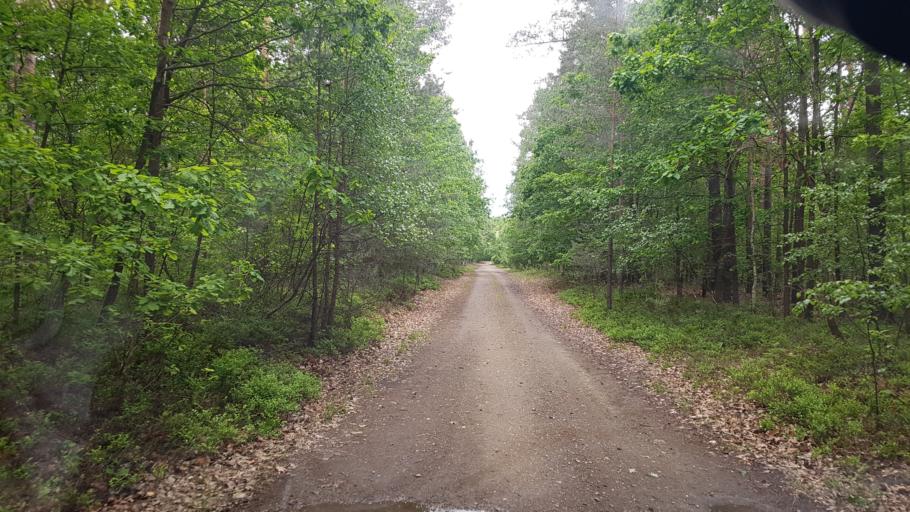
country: DE
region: Brandenburg
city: Hohenleipisch
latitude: 51.5291
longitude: 13.5407
